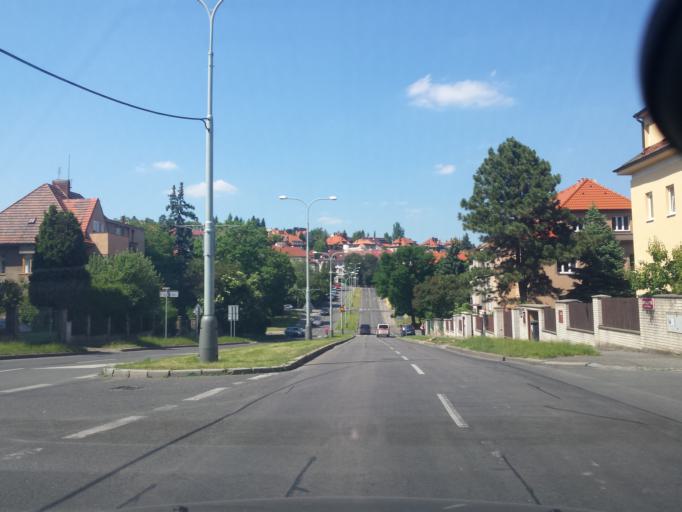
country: CZ
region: Praha
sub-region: Praha 1
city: Mala Strana
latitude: 50.0969
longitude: 14.3724
